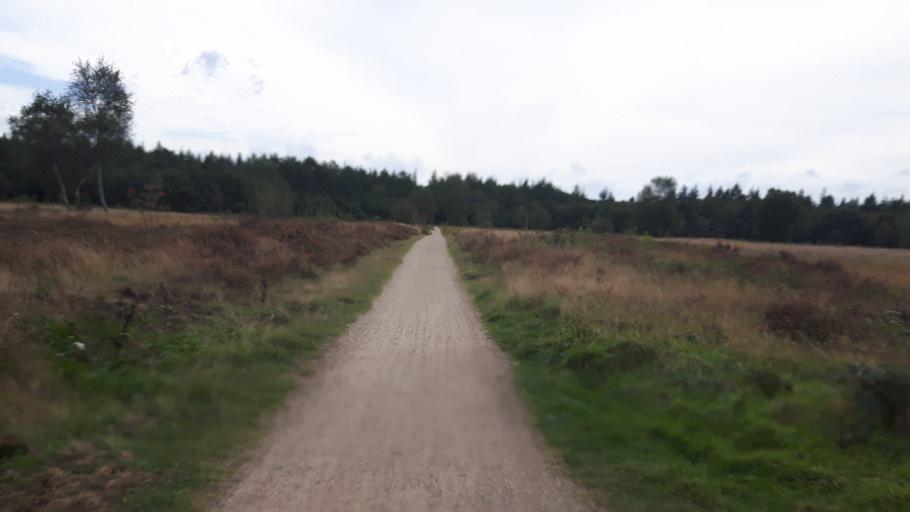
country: NL
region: Gelderland
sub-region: Gemeente Ermelo
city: Ermelo
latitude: 52.2841
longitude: 5.6145
